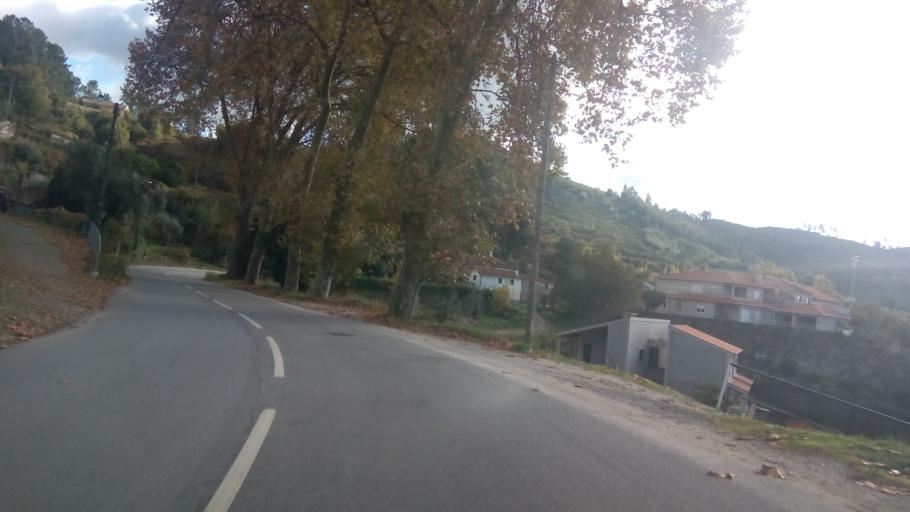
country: PT
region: Porto
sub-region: Amarante
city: Amarante
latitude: 41.2653
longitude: -8.0127
